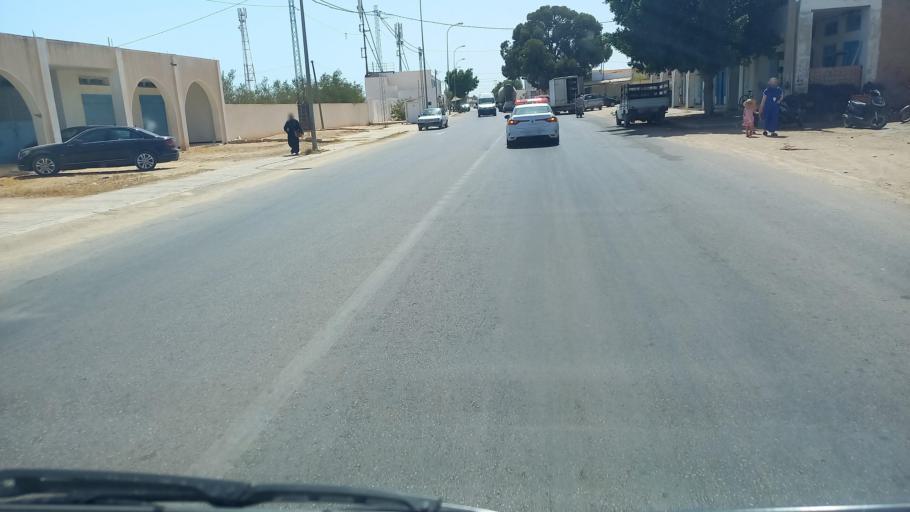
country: TN
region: Madanin
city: Midoun
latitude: 33.7767
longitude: 10.8937
